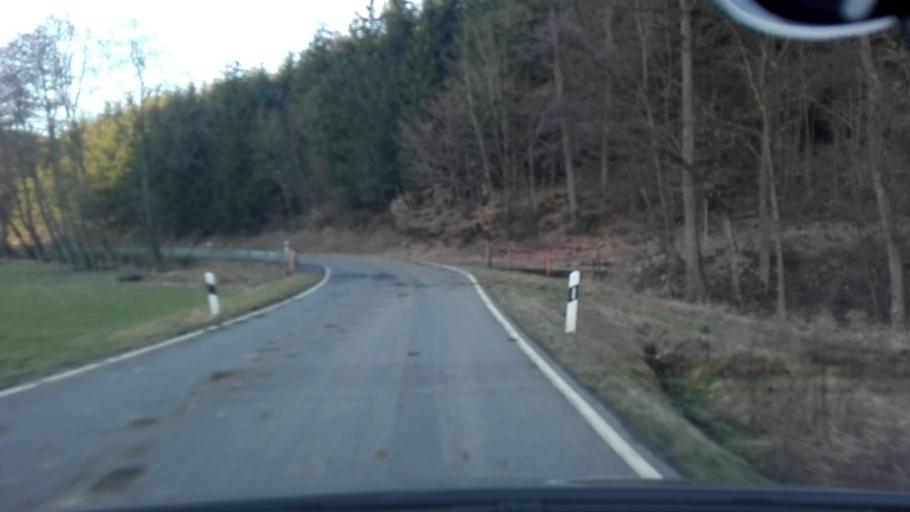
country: DE
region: North Rhine-Westphalia
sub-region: Regierungsbezirk Arnsberg
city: Lennestadt
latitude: 51.1943
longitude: 8.0703
